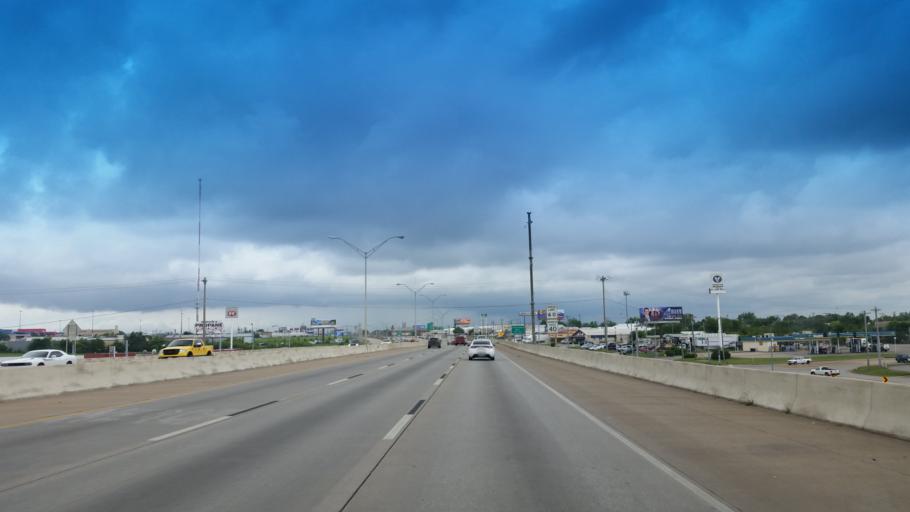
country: US
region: Oklahoma
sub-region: Oklahoma County
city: Del City
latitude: 35.4077
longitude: -97.4936
